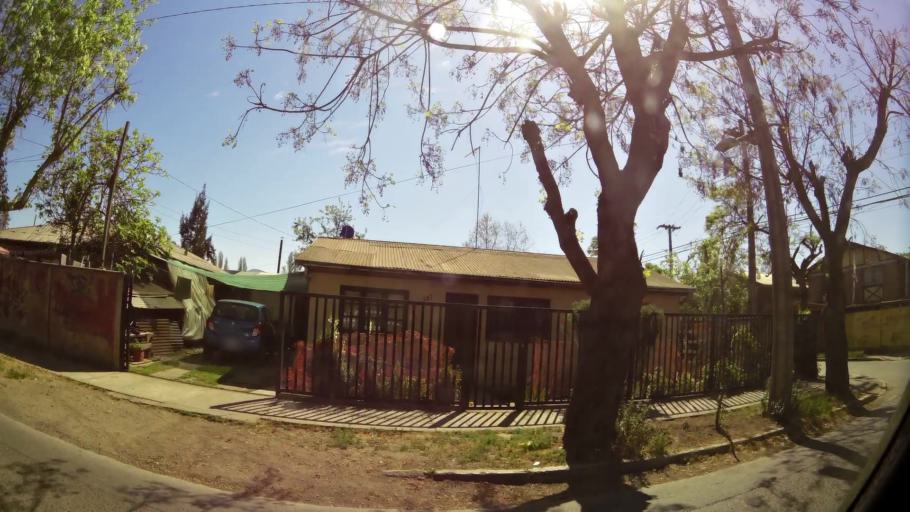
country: CL
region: Santiago Metropolitan
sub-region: Provincia de Talagante
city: Penaflor
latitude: -33.6003
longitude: -70.8825
